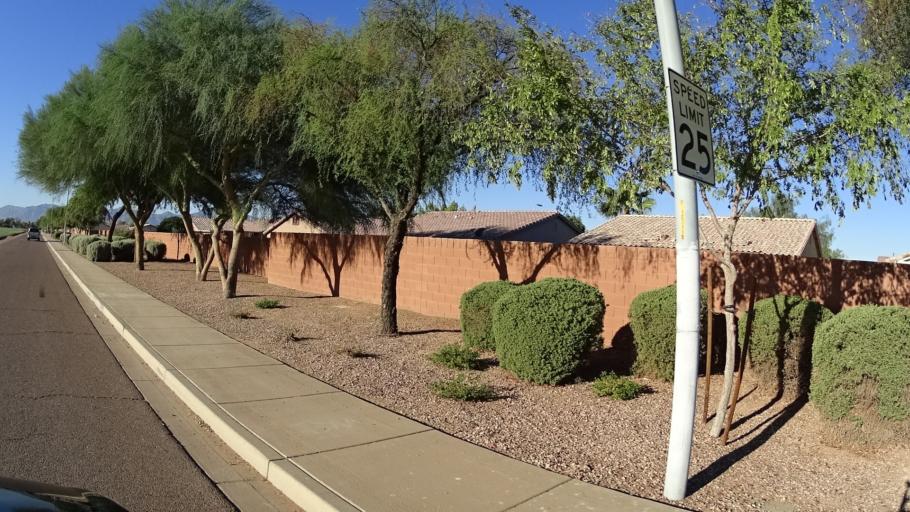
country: US
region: Arizona
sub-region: Maricopa County
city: Tolleson
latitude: 33.4294
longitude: -112.2125
